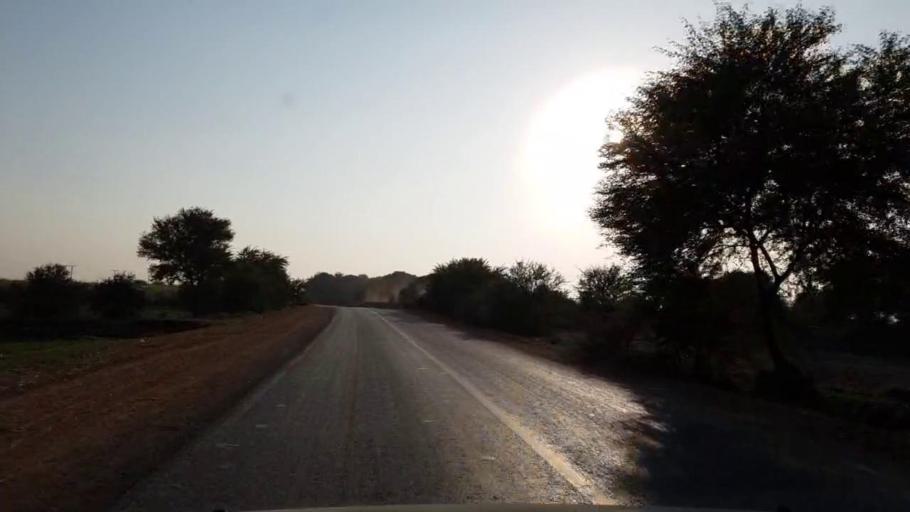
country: PK
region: Sindh
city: Daro Mehar
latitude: 24.6569
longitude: 68.1305
